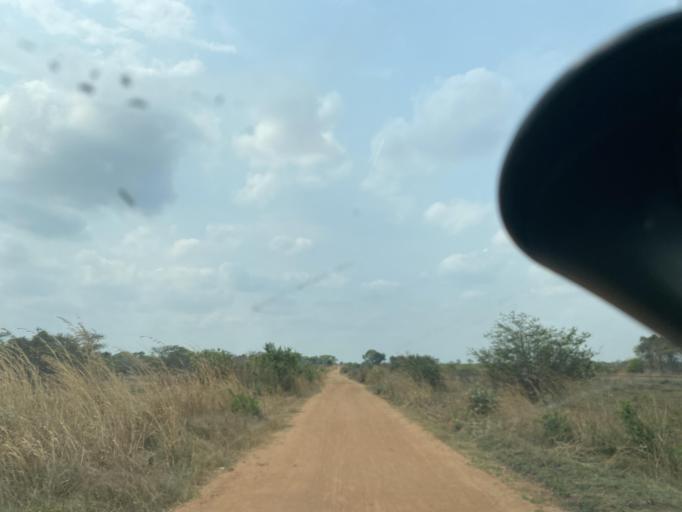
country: ZM
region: Lusaka
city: Lusaka
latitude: -15.1424
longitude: 28.3667
